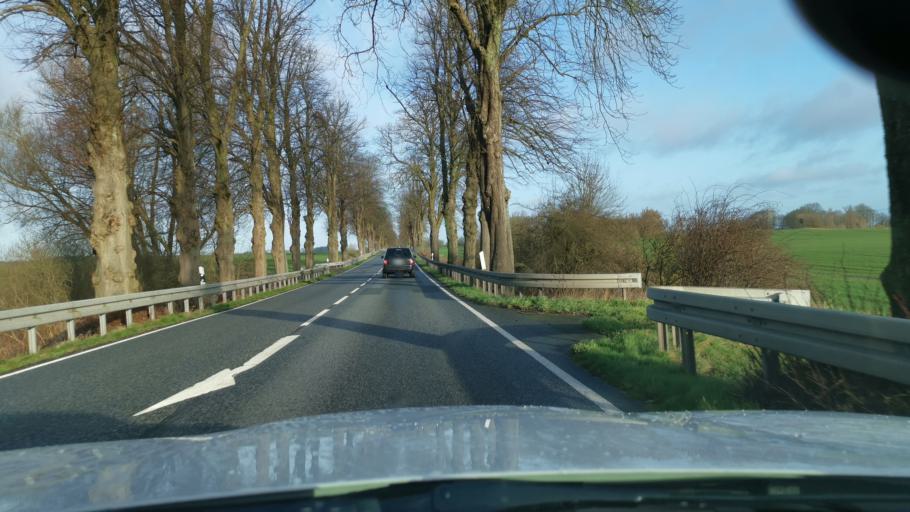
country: DE
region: Mecklenburg-Vorpommern
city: Laage
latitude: 53.9458
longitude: 12.3094
